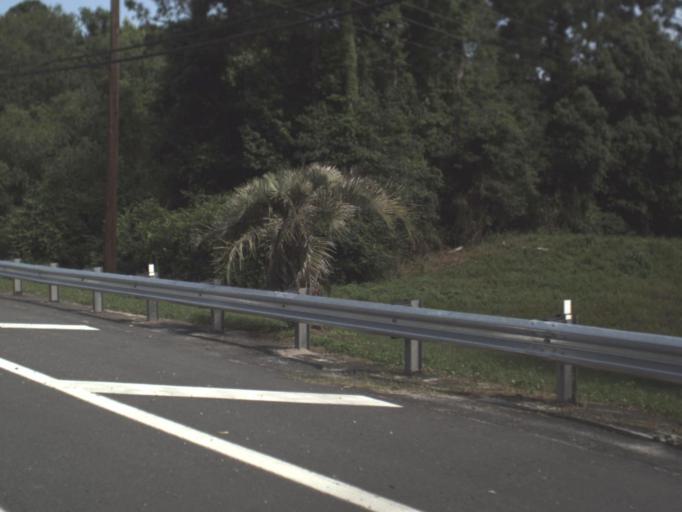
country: US
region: Florida
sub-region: Bradford County
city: Starke
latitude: 29.9423
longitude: -82.1031
